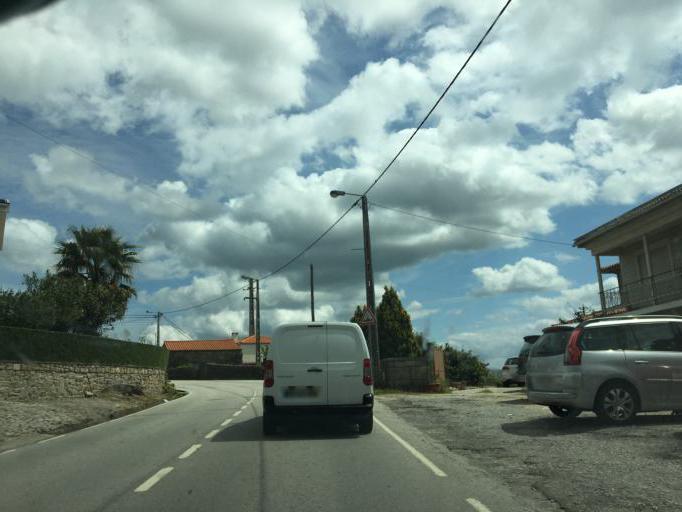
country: PT
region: Vila Real
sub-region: Boticas
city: Boticas
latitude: 41.7085
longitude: -7.6410
